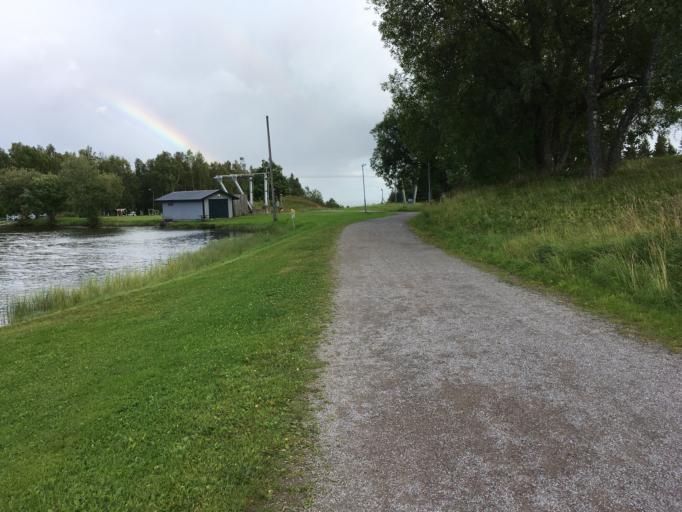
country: SE
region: Vaestra Goetaland
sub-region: Falkopings Kommun
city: Falkoeping
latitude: 58.1740
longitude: 13.5215
